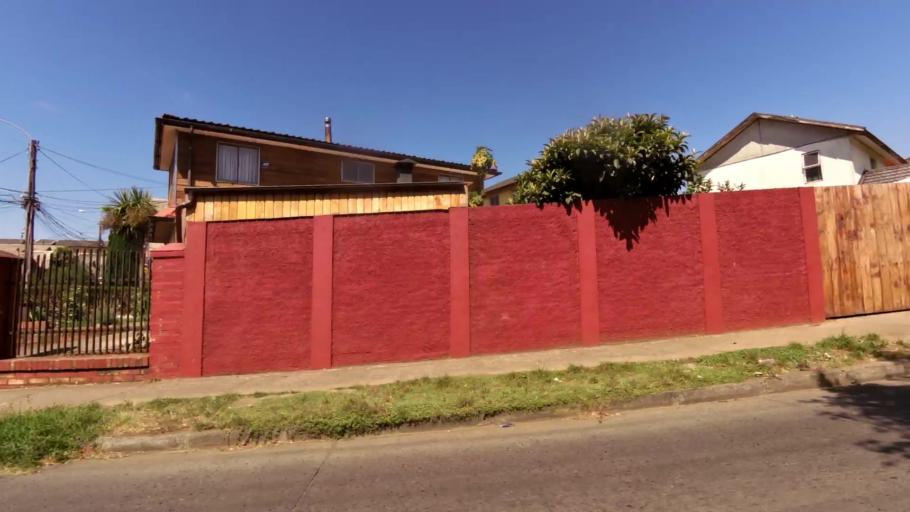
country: CL
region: Biobio
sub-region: Provincia de Concepcion
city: Concepcion
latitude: -36.7837
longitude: -73.0425
